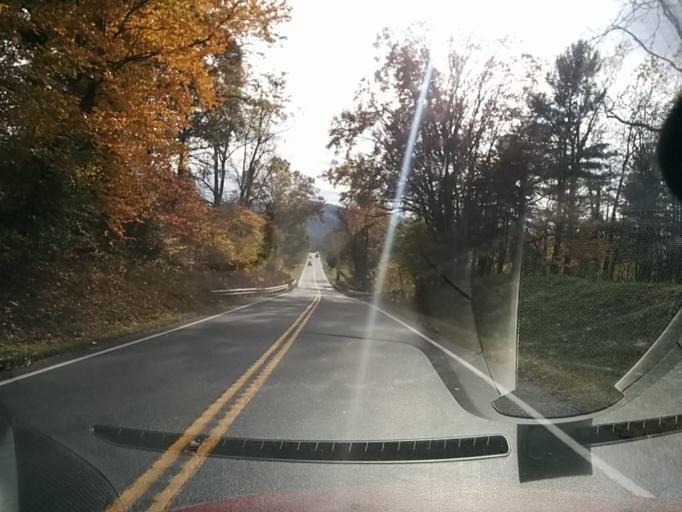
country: US
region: Virginia
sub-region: Nelson County
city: Nellysford
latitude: 37.8806
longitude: -78.9072
